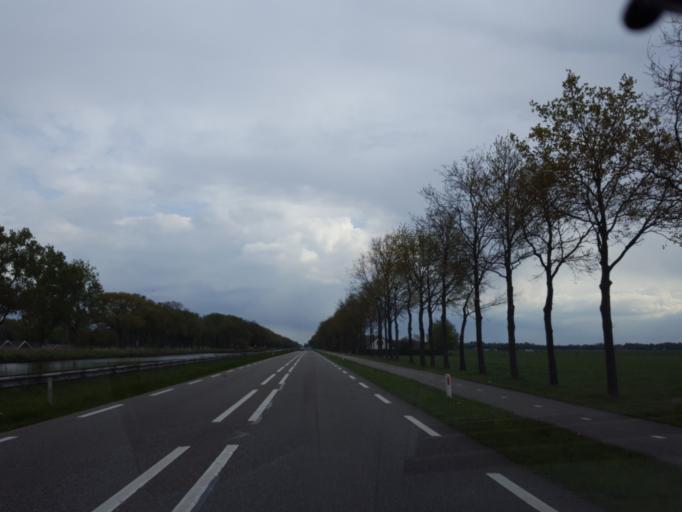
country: NL
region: Limburg
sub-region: Gemeente Nederweert
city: Nederweert
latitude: 51.3242
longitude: 5.7474
